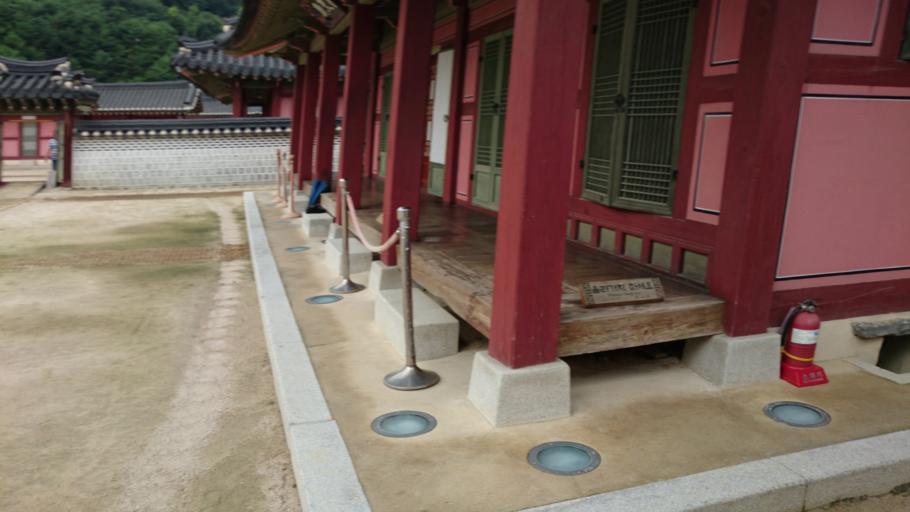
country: KR
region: Gyeonggi-do
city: Suwon-si
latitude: 37.2817
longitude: 127.0144
